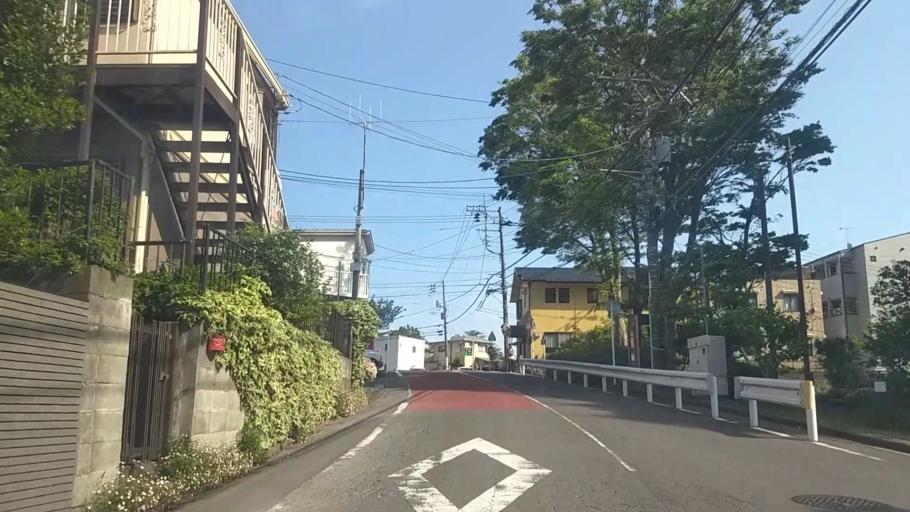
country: JP
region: Kanagawa
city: Fujisawa
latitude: 35.3448
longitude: 139.4900
